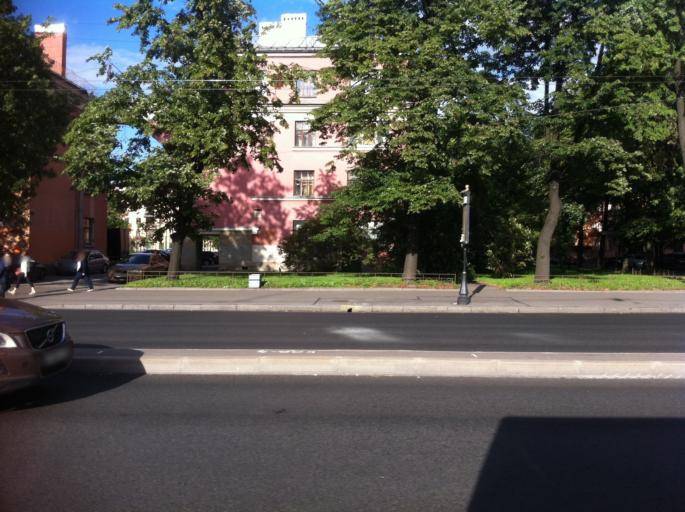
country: RU
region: St.-Petersburg
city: Admiralteisky
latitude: 59.8982
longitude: 30.2759
